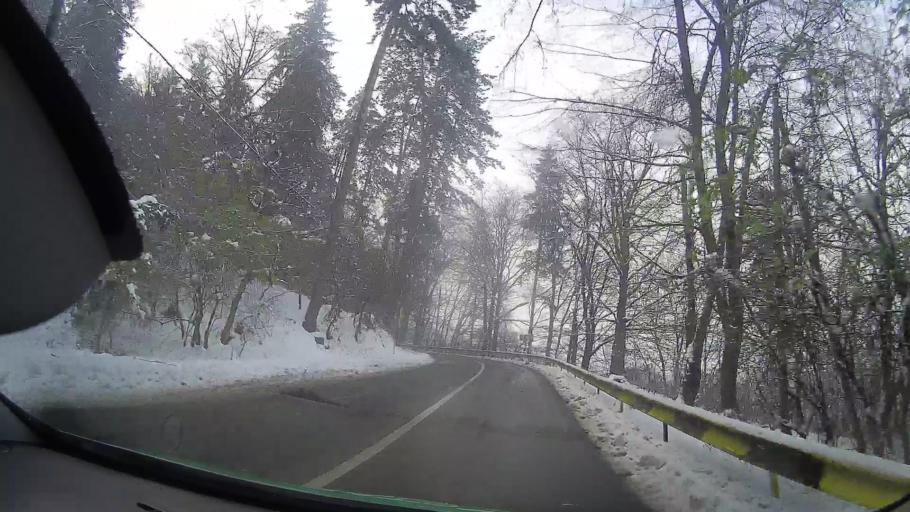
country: RO
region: Neamt
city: Piatra Neamt
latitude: 46.9240
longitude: 26.3576
